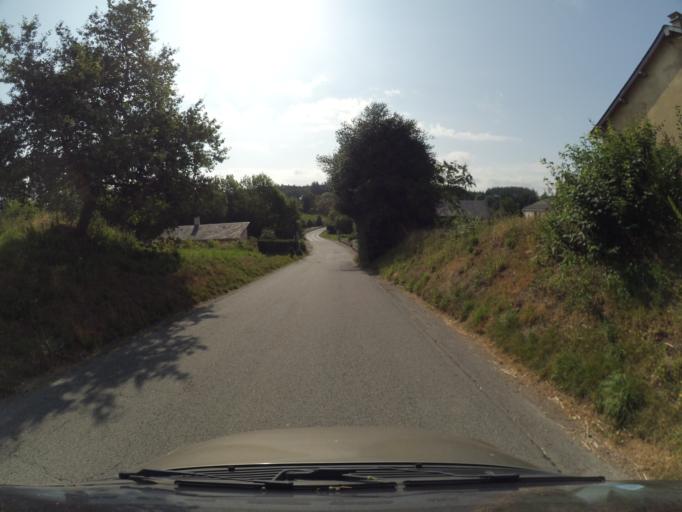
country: FR
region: Limousin
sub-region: Departement de la Correze
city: Meymac
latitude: 45.6408
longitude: 2.0959
